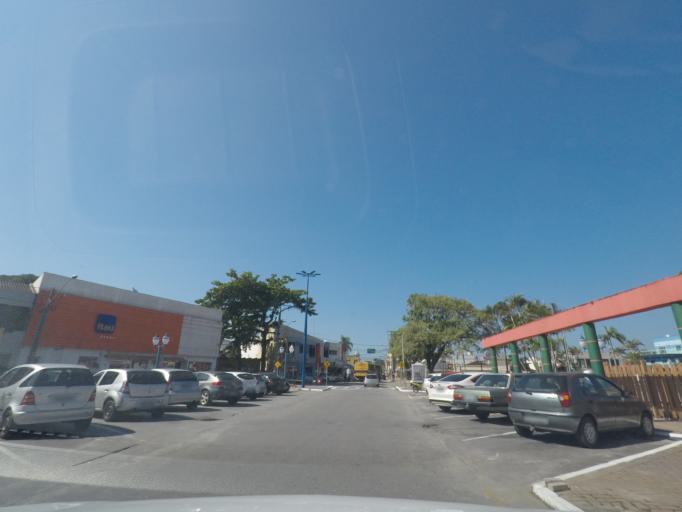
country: BR
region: Parana
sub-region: Guaratuba
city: Guaratuba
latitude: -25.8184
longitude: -48.5346
